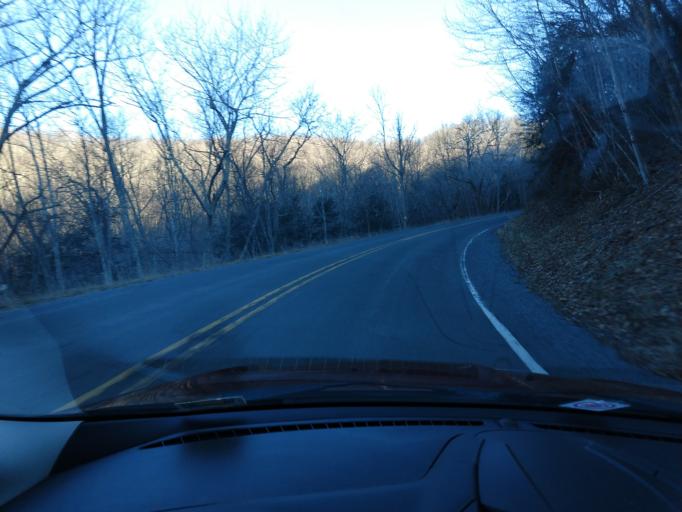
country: US
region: Virginia
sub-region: Highland County
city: Monterey
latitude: 38.4576
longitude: -79.6636
